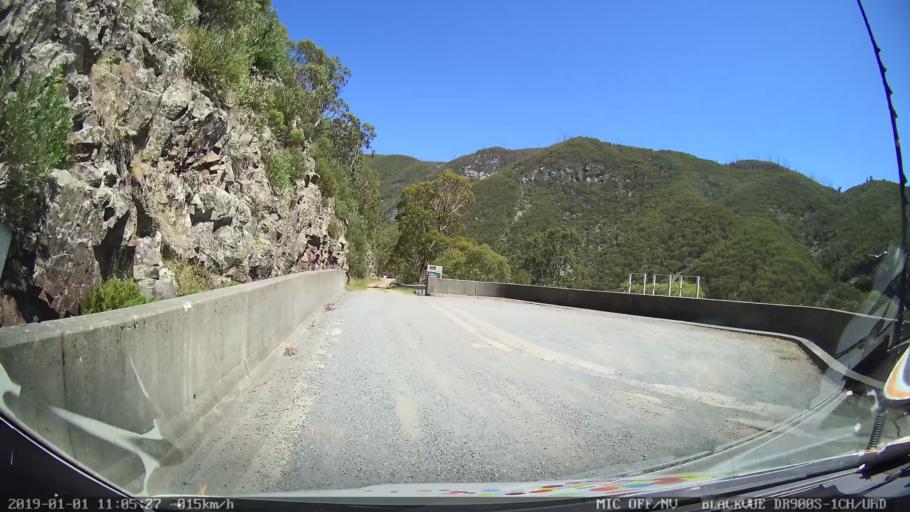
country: AU
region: New South Wales
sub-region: Snowy River
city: Jindabyne
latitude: -35.9658
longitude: 148.3893
